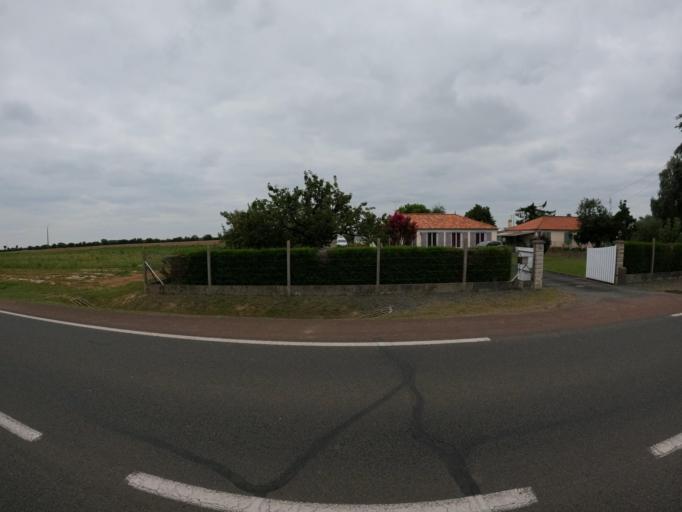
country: FR
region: Pays de la Loire
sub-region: Departement de la Vendee
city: Saint-Hilaire-des-Loges
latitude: 46.4085
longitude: -0.6831
